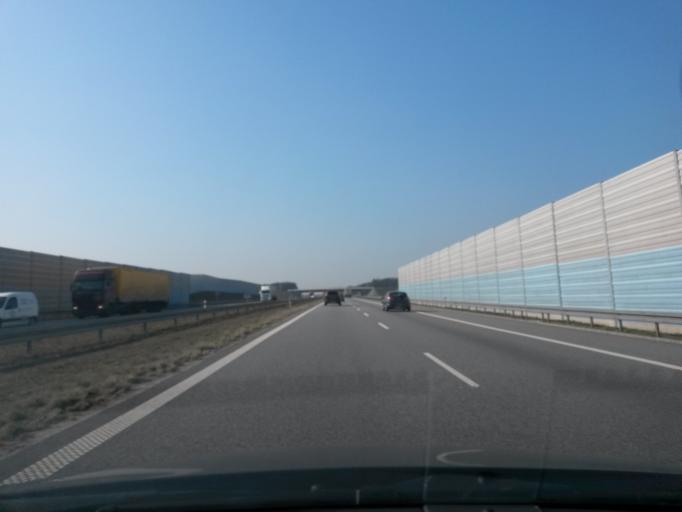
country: PL
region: Lodz Voivodeship
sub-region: powiat Lowicki
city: Lyszkowice
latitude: 51.9681
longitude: 19.8642
